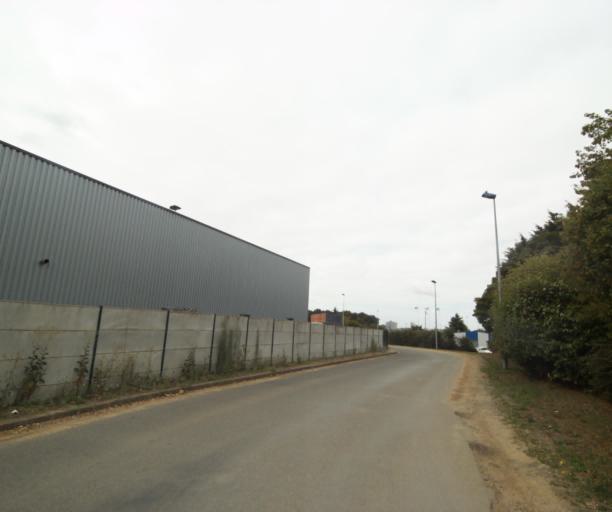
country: FR
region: Pays de la Loire
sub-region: Departement de la Sarthe
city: Sable-sur-Sarthe
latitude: 47.8270
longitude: -0.3128
